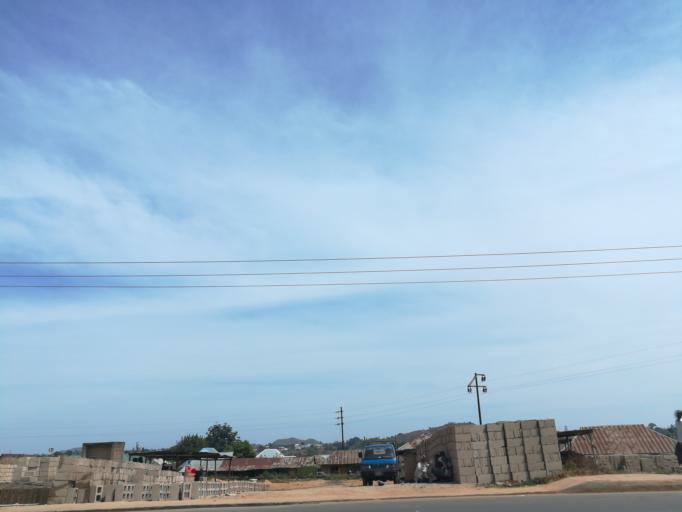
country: NG
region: Plateau
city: Bukuru
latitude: 9.7644
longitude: 8.8598
